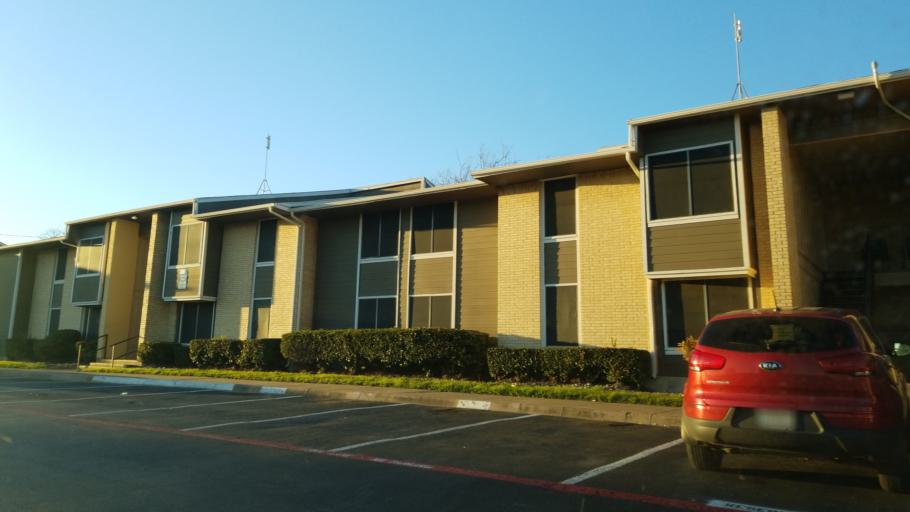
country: US
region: Texas
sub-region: Dallas County
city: Grand Prairie
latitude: 32.7271
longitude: -97.0483
